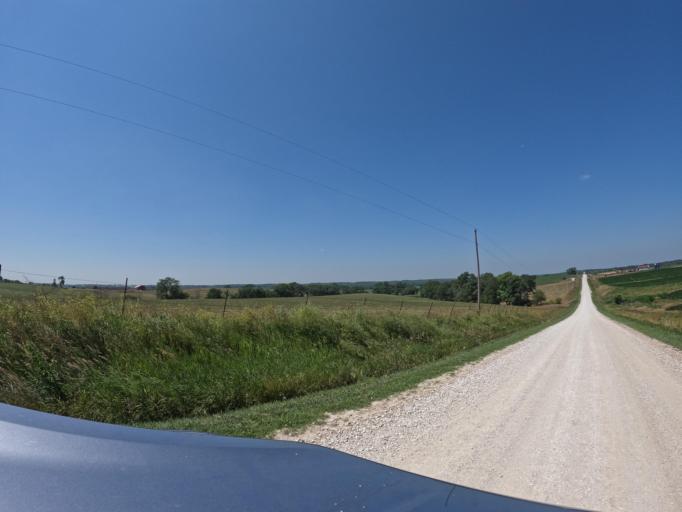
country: US
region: Iowa
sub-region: Keokuk County
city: Sigourney
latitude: 41.2505
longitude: -92.2098
